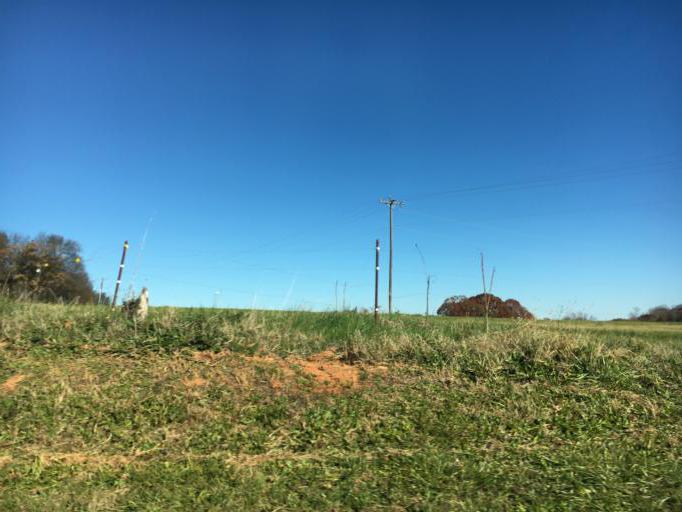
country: US
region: South Carolina
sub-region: Spartanburg County
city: Roebuck
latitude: 34.8397
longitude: -81.9991
